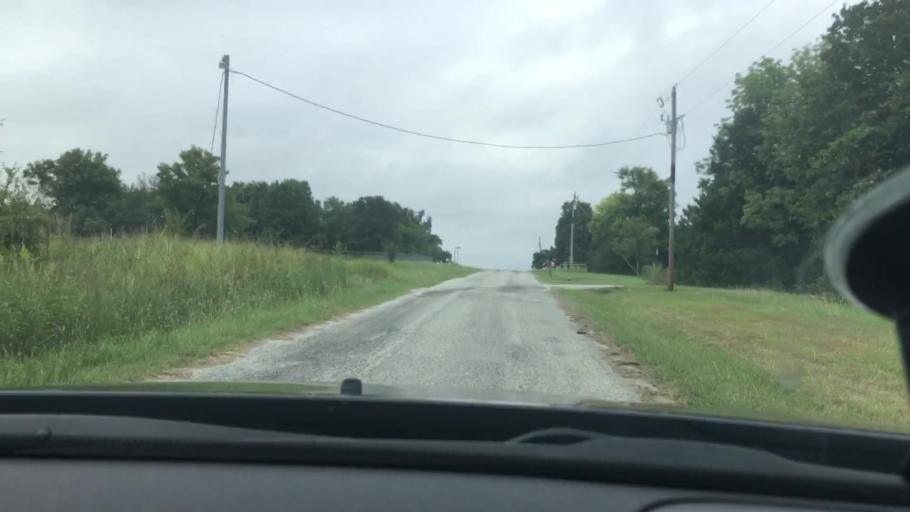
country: US
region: Oklahoma
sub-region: Pontotoc County
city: Byng
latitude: 34.8102
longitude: -96.5475
